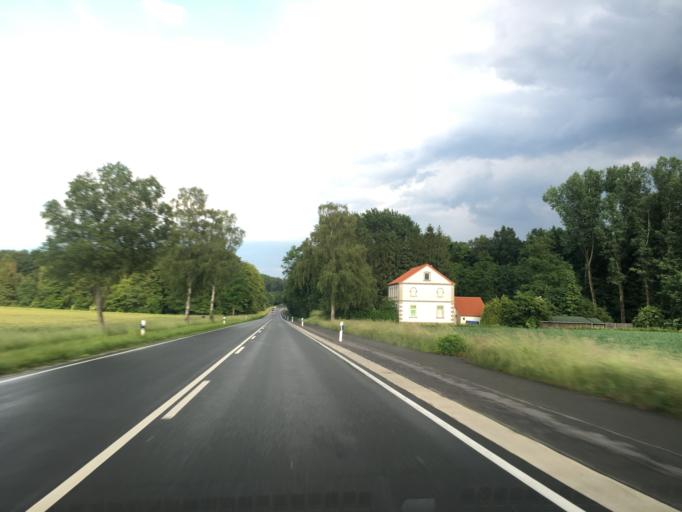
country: DE
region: North Rhine-Westphalia
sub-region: Regierungsbezirk Munster
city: Steinfurt
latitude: 52.1338
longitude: 7.3761
